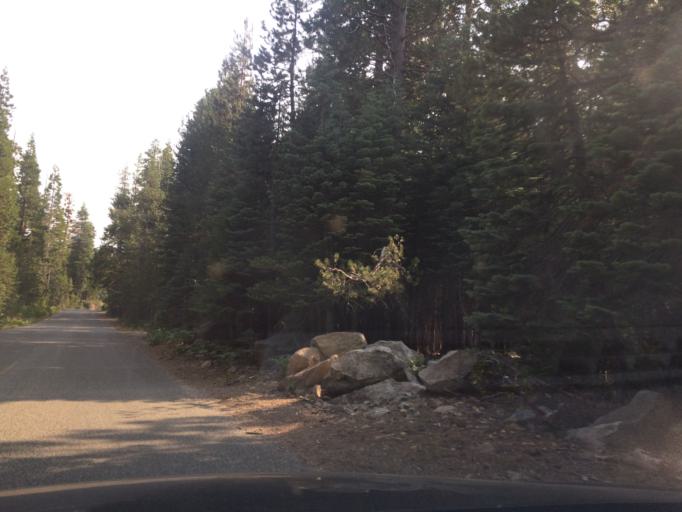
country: US
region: California
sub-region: Sierra County
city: Downieville
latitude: 39.3898
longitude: -120.6698
